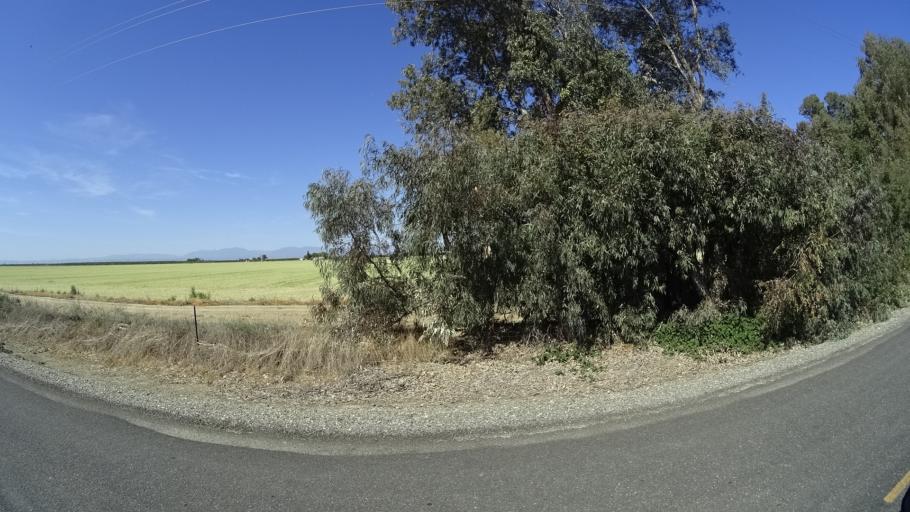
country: US
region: California
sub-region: Glenn County
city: Hamilton City
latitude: 39.6590
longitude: -122.1035
